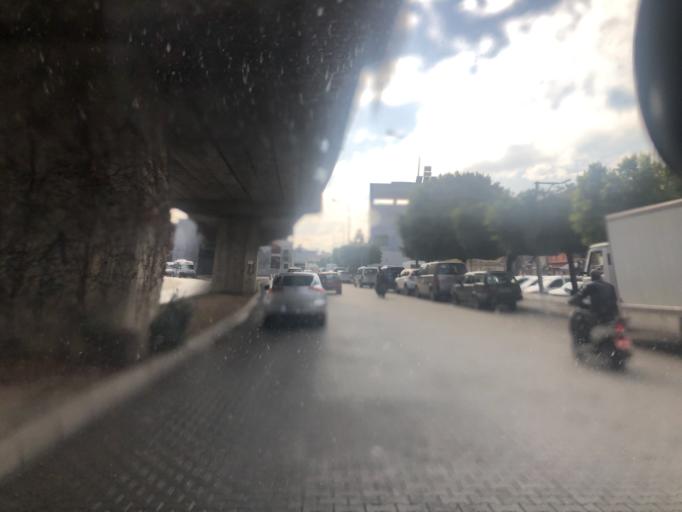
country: TR
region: Adana
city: Seyhan
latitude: 36.9862
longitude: 35.3186
